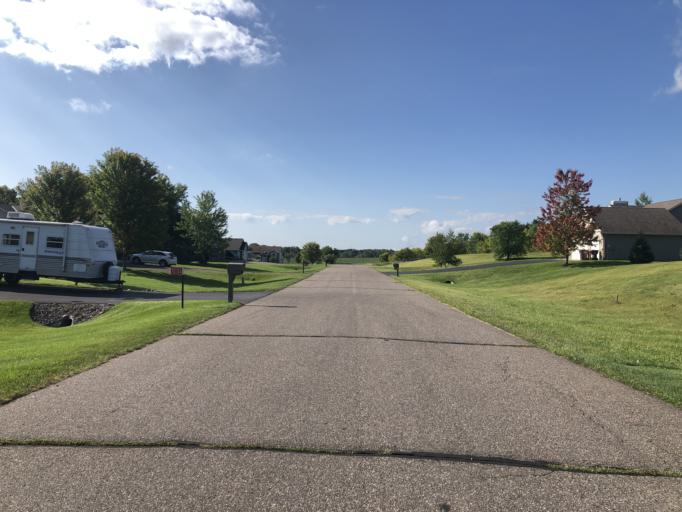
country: US
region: Minnesota
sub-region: Sherburne County
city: Becker
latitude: 45.4229
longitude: -93.8360
